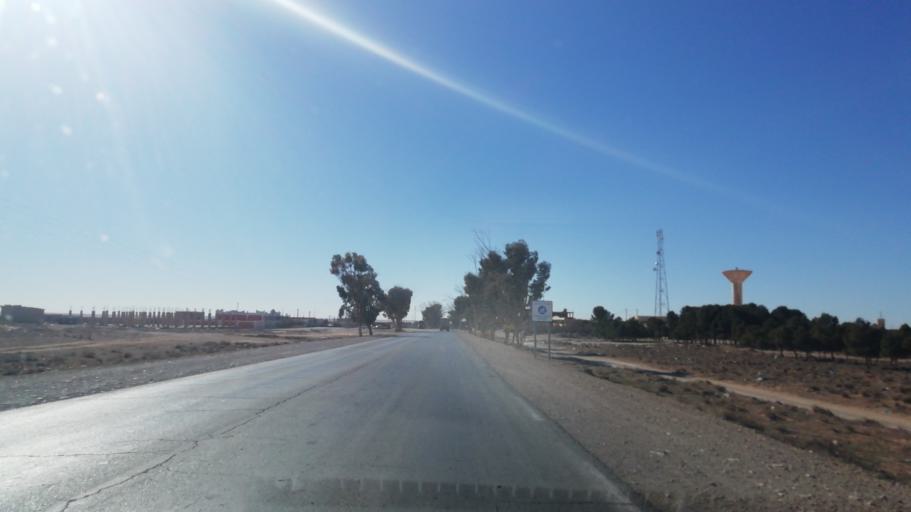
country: DZ
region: Saida
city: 'Ain el Hadjar
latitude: 34.1591
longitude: 0.0712
